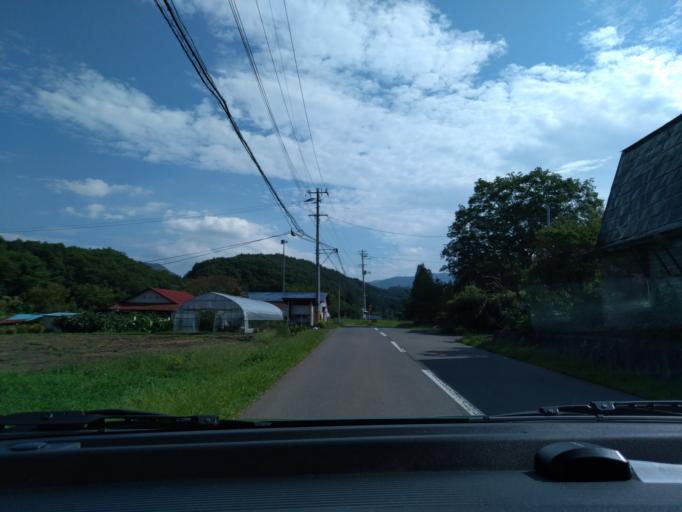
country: JP
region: Iwate
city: Shizukuishi
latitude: 39.6486
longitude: 140.9931
